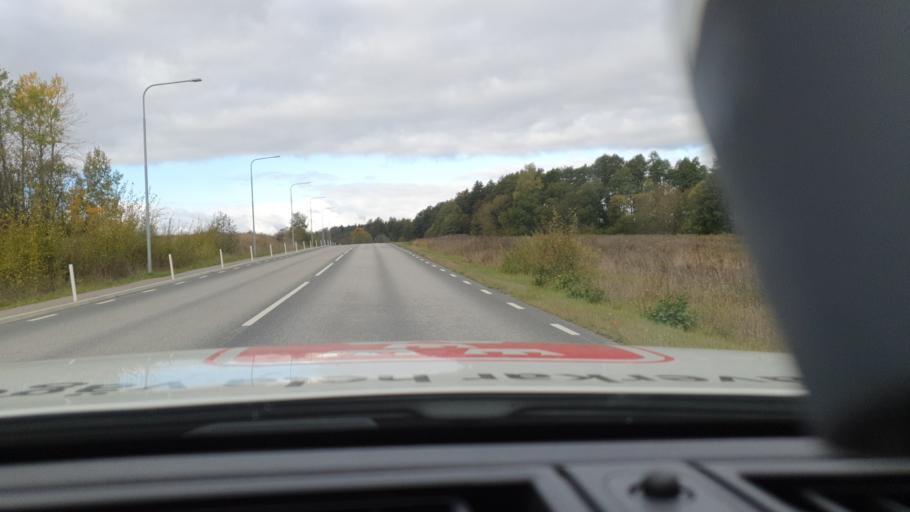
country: SE
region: Stockholm
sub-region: Upplands-Bro Kommun
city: Bro
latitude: 59.5109
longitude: 17.6266
